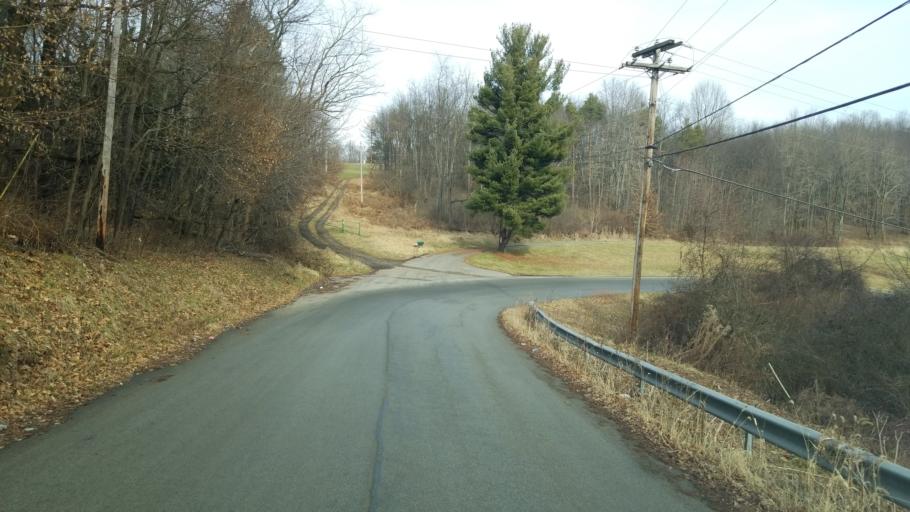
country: US
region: Pennsylvania
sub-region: Indiana County
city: Chevy Chase Heights
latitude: 40.6422
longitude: -79.1233
